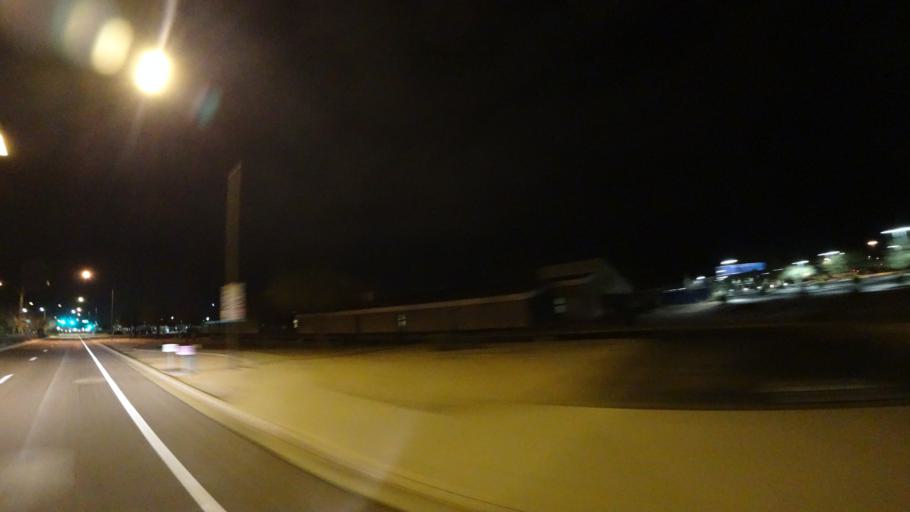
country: US
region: Arizona
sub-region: Maricopa County
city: Queen Creek
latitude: 33.2932
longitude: -111.7037
